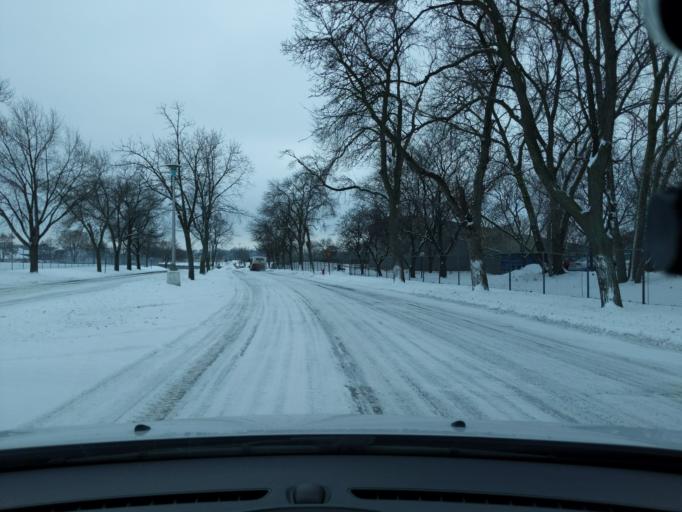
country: US
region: Minnesota
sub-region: Ramsey County
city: Falcon Heights
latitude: 44.9825
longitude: -93.1795
